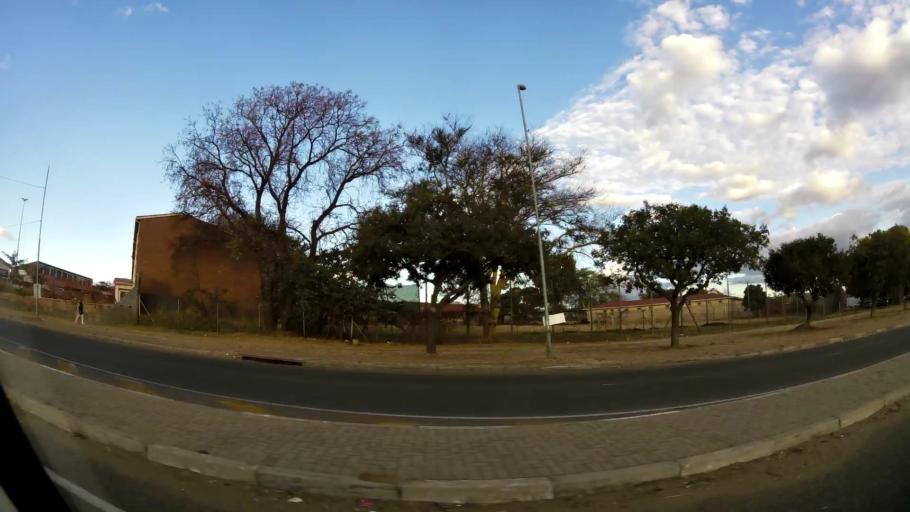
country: ZA
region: Limpopo
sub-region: Capricorn District Municipality
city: Polokwane
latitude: -23.8957
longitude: 29.4505
